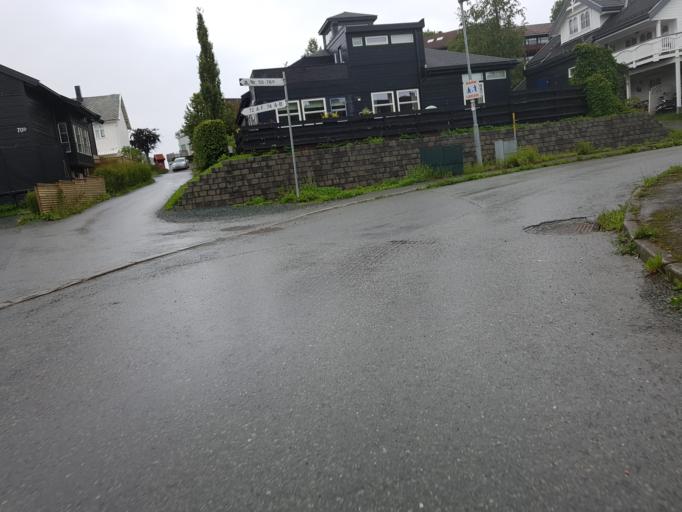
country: NO
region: Sor-Trondelag
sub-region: Trondheim
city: Trondheim
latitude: 63.4026
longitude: 10.4487
